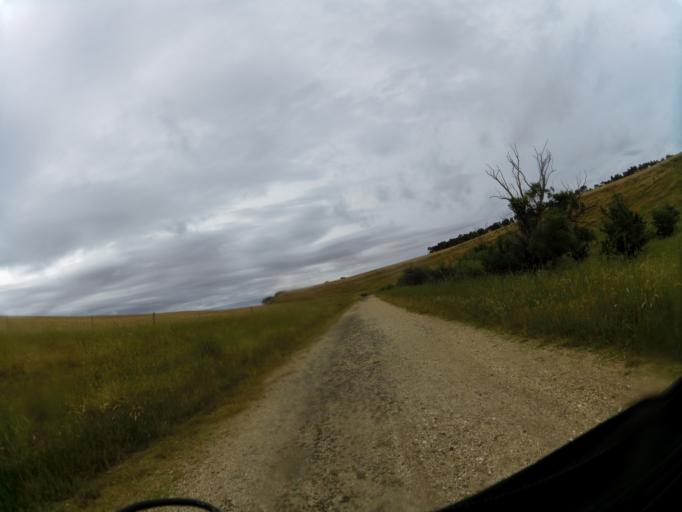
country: AU
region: Victoria
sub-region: Mount Alexander
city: Castlemaine
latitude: -37.2061
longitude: 144.0235
